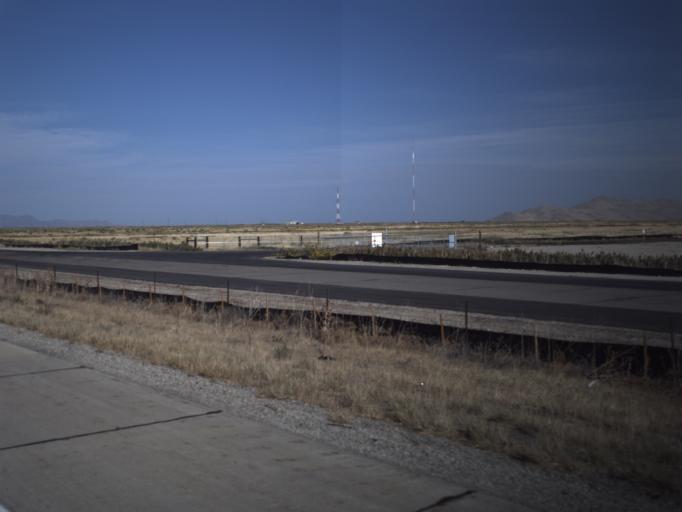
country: US
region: Utah
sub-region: Salt Lake County
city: Magna
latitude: 40.7711
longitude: -112.0840
